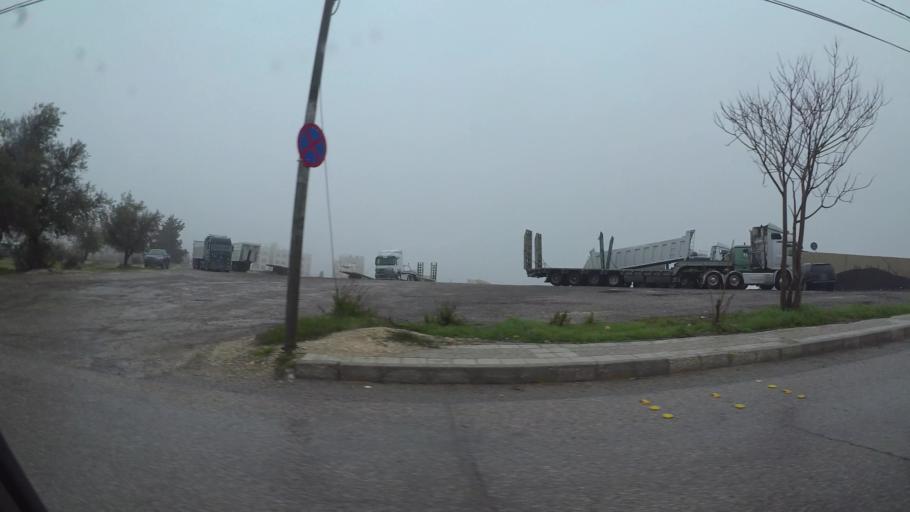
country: JO
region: Amman
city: Al Jubayhah
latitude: 32.0283
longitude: 35.8301
